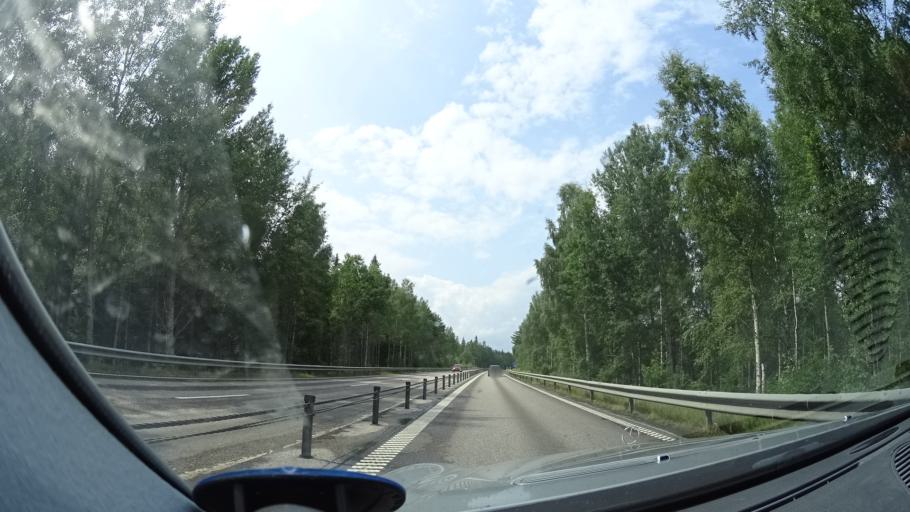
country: SE
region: Kalmar
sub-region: Nybro Kommun
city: Nybro
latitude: 56.7258
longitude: 15.9054
